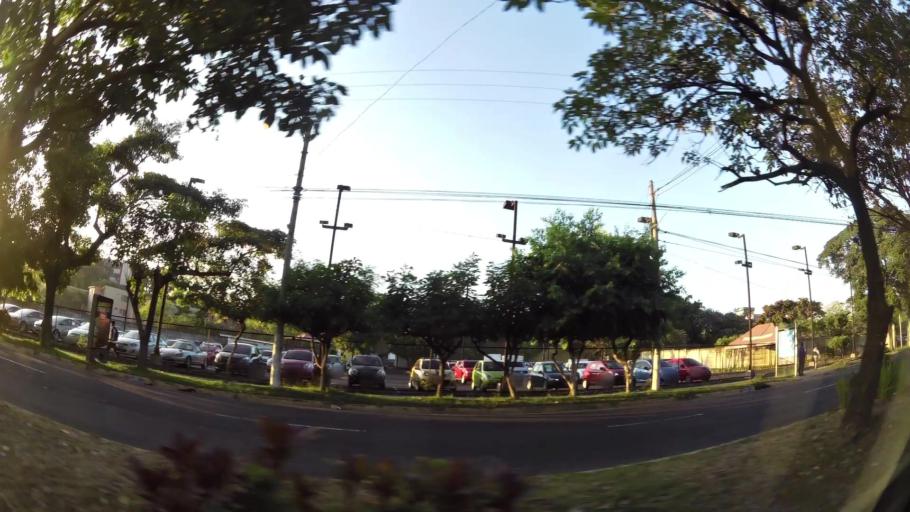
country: SV
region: San Salvador
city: San Salvador
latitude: 13.7042
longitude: -89.2184
